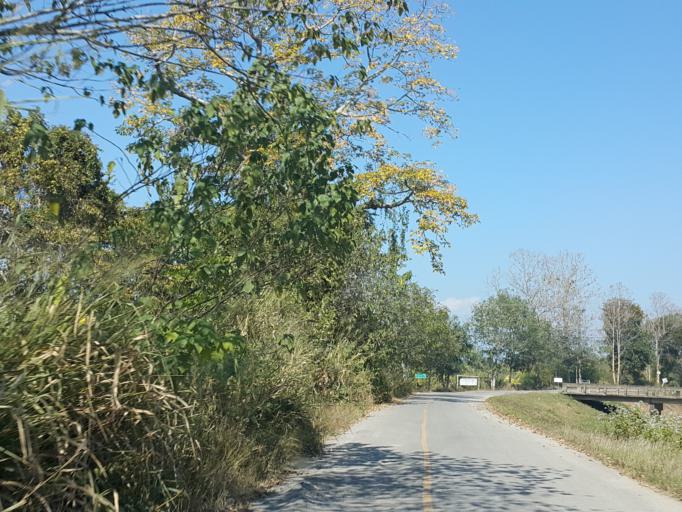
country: TH
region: Chiang Mai
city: Mae Taeng
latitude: 19.0905
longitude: 98.9500
